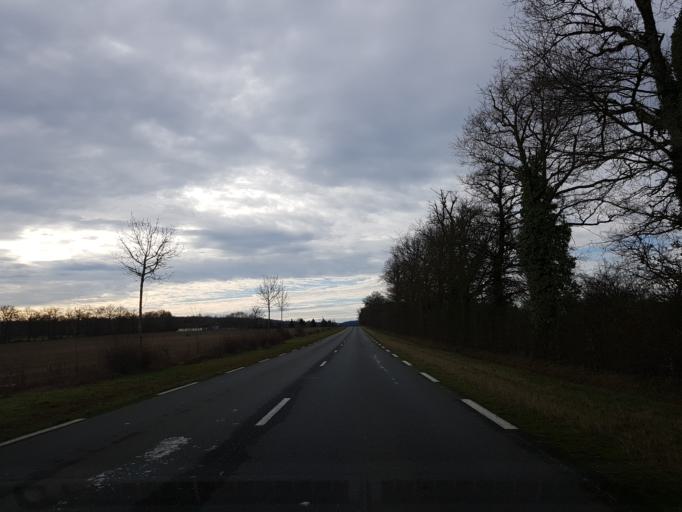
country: FR
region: Limousin
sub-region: Departement de la Haute-Vienne
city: Bellac
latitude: 46.0614
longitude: 0.9798
